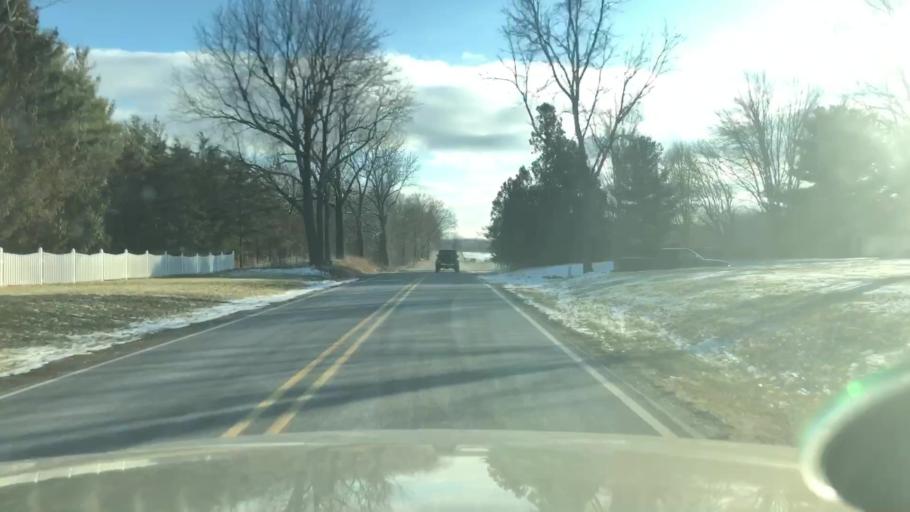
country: US
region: Michigan
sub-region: Jackson County
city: Vandercook Lake
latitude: 42.1049
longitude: -84.4512
